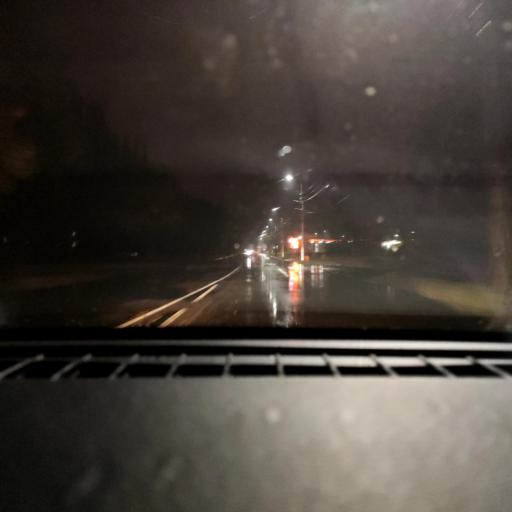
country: RU
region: Voronezj
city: Maslovka
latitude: 51.6014
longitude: 39.2368
